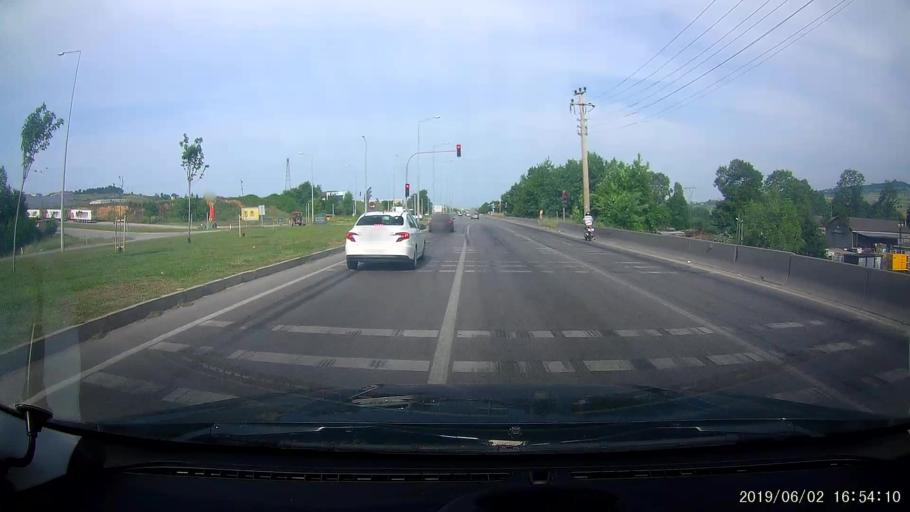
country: TR
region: Samsun
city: Samsun
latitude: 41.2917
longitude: 36.2357
